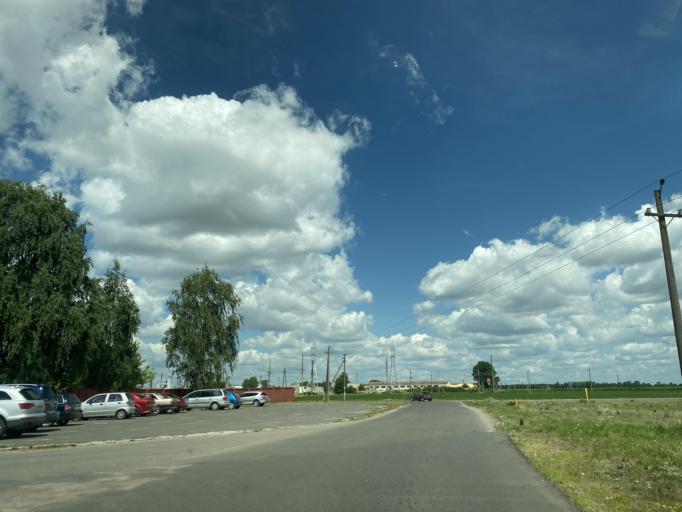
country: BY
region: Brest
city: Ivanava
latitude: 52.1387
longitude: 25.5521
